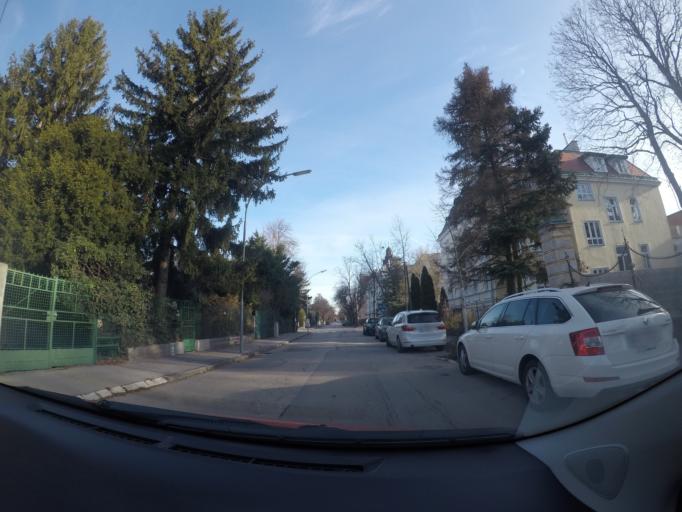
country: AT
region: Lower Austria
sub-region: Politischer Bezirk Baden
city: Baden
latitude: 48.0035
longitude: 16.2238
